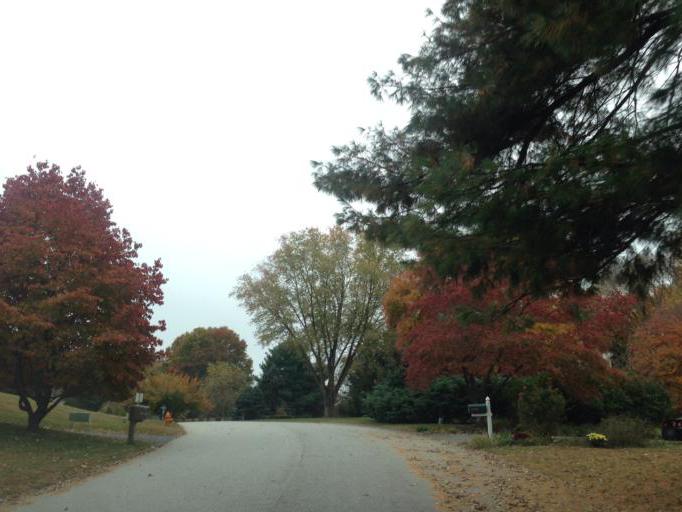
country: US
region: Maryland
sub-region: Howard County
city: Ellicott City
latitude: 39.3057
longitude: -76.8380
